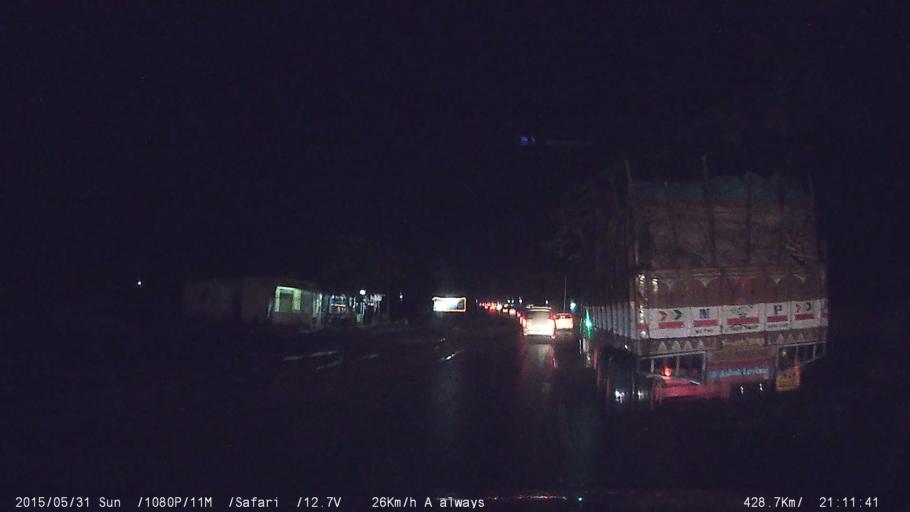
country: IN
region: Karnataka
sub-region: Ramanagara
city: Channapatna
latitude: 12.6753
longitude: 77.2247
